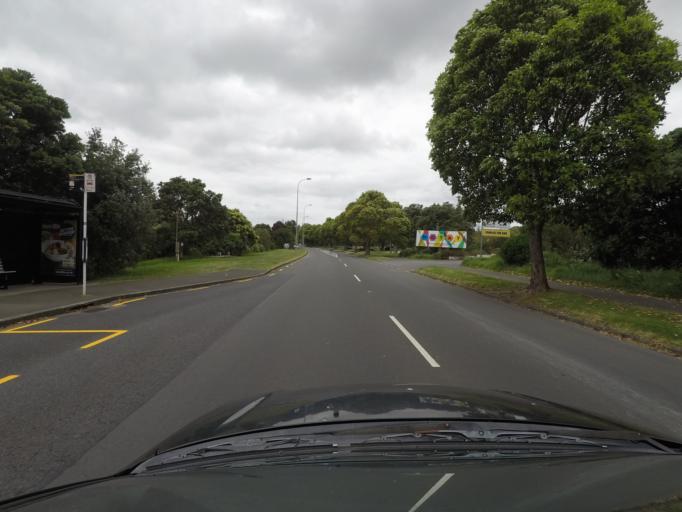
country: NZ
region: Auckland
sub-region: Auckland
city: Rosebank
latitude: -36.8590
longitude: 174.7150
